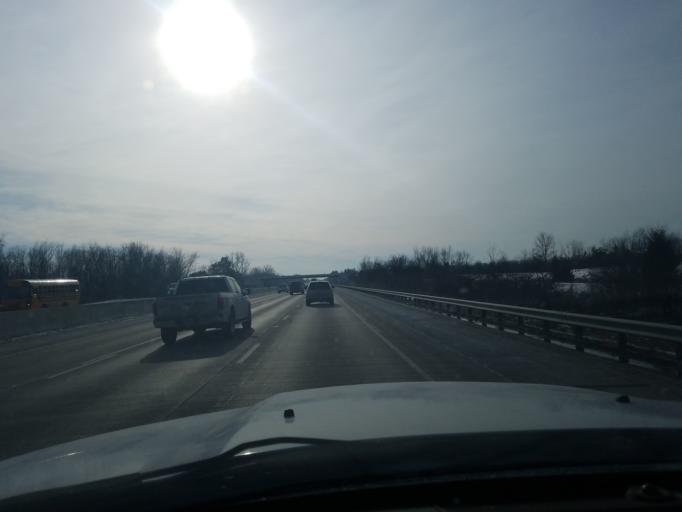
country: US
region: Indiana
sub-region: Allen County
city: Fort Wayne
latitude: 41.1058
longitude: -85.2040
